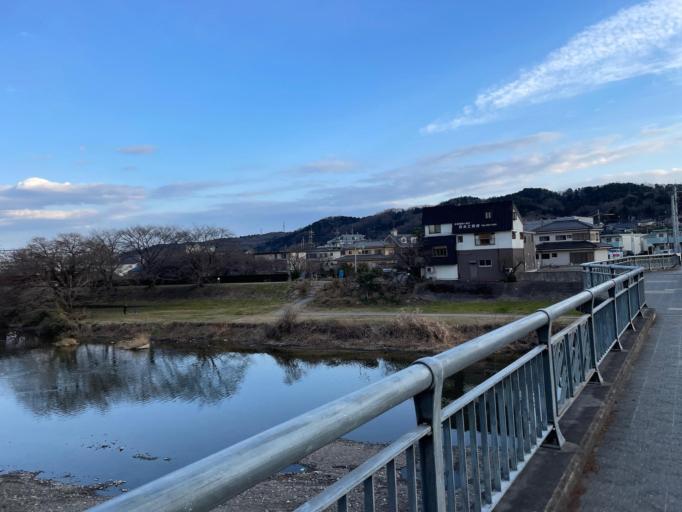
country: JP
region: Saitama
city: Hanno
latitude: 35.8386
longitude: 139.3477
